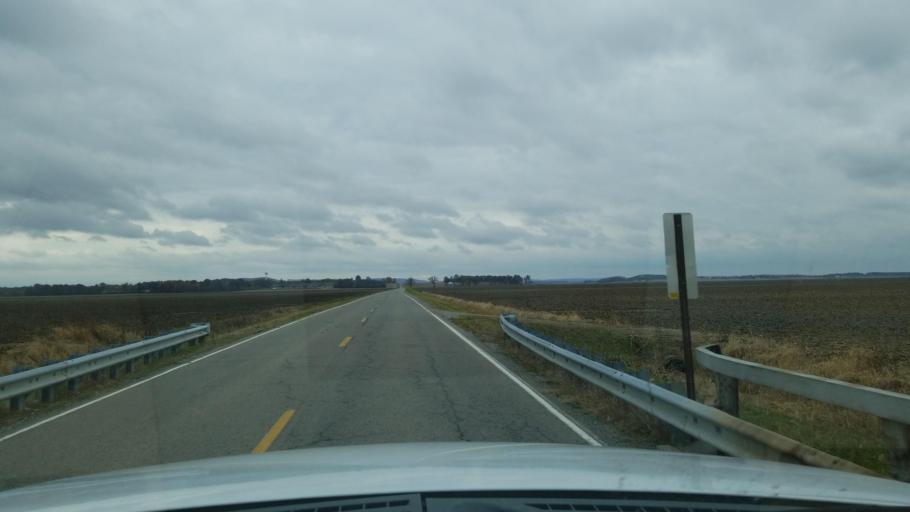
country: US
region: Illinois
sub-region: Saline County
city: Eldorado
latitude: 37.7721
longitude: -88.4382
